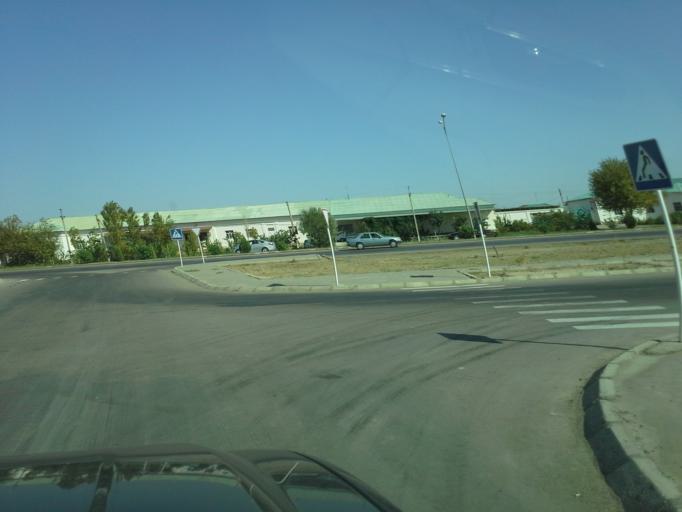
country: TM
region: Dasoguz
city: Dasoguz
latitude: 41.8193
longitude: 59.9614
